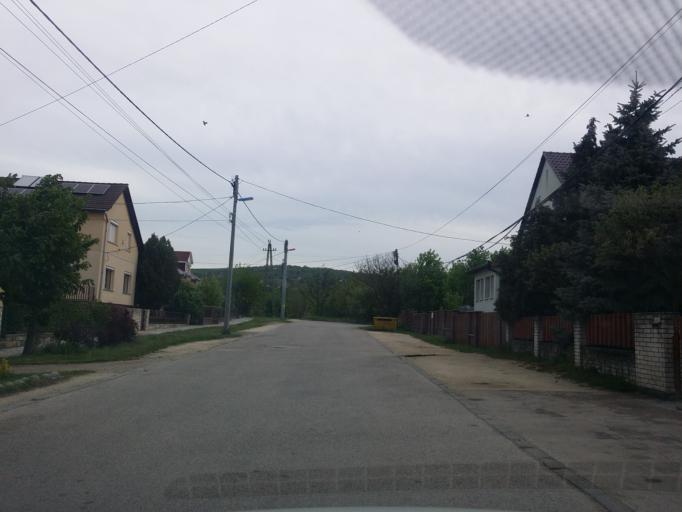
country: HU
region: Pest
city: Biatorbagy
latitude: 47.4787
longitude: 18.8337
